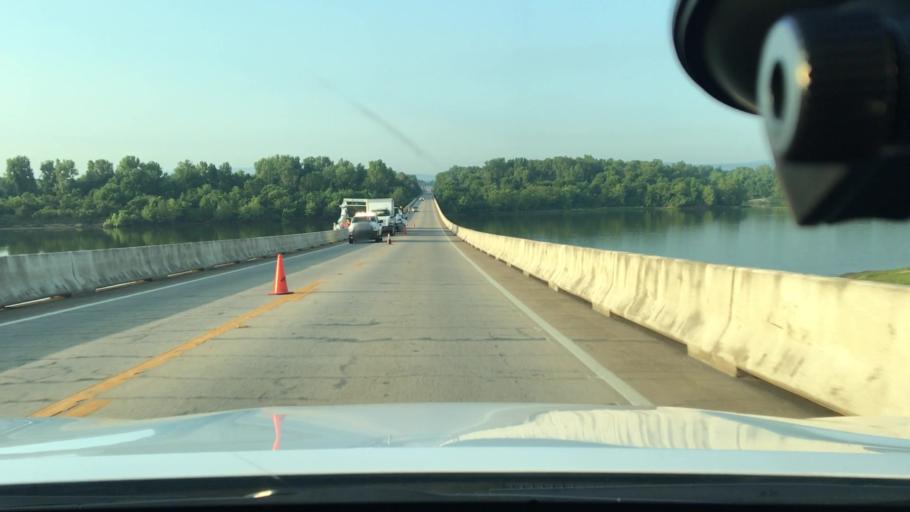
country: US
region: Arkansas
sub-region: Johnson County
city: Clarksville
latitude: 35.4087
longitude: -93.5319
